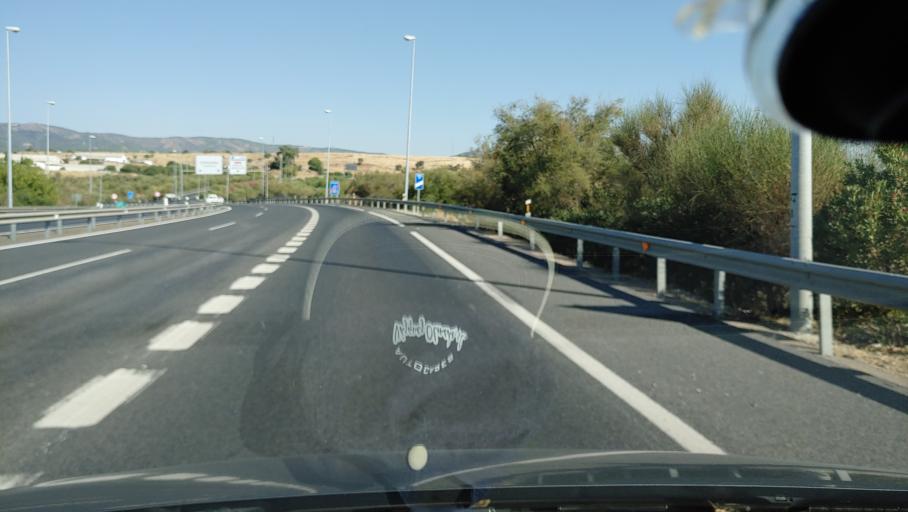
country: ES
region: Andalusia
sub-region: Province of Cordoba
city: Cordoba
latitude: 37.9046
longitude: -4.7512
